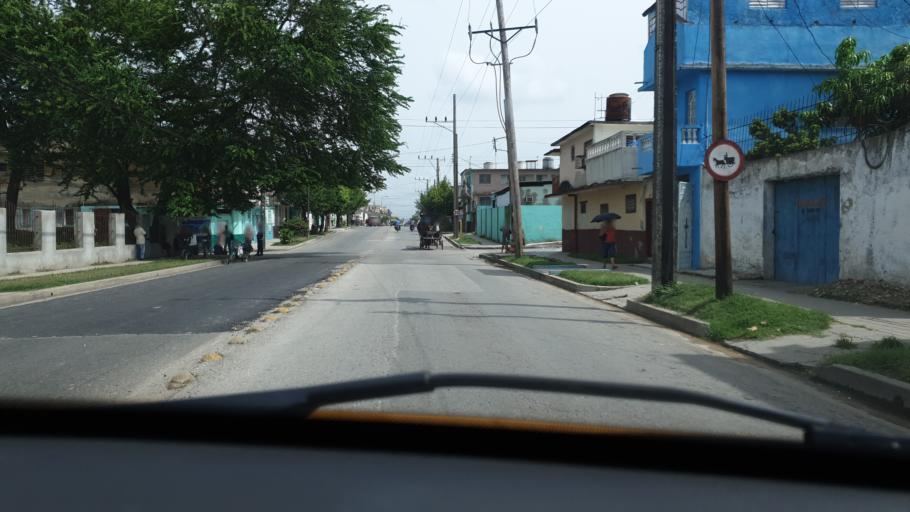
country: CU
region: Villa Clara
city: Santa Clara
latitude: 22.3942
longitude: -79.9618
